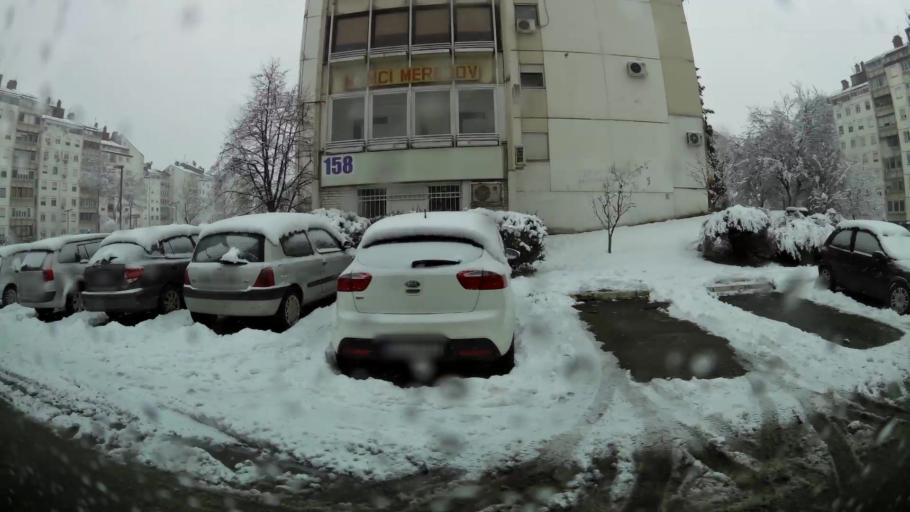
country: RS
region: Central Serbia
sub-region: Belgrade
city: Cukarica
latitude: 44.7954
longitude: 20.3727
